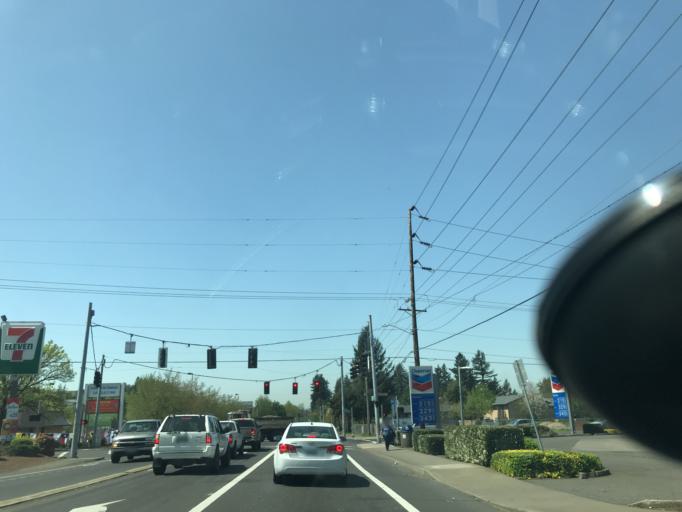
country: US
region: Oregon
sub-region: Multnomah County
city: Gresham
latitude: 45.4922
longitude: -122.4841
